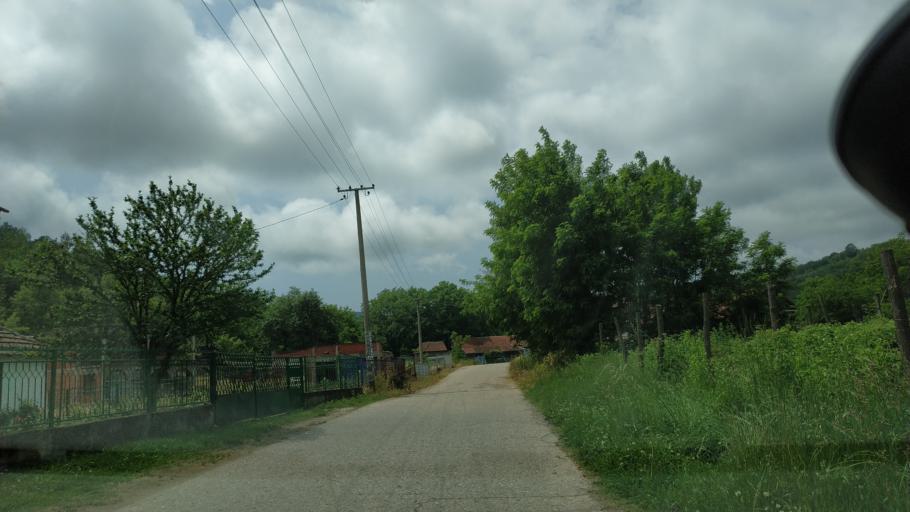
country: RS
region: Central Serbia
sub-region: Nisavski Okrug
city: Aleksinac
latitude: 43.4246
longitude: 21.7085
